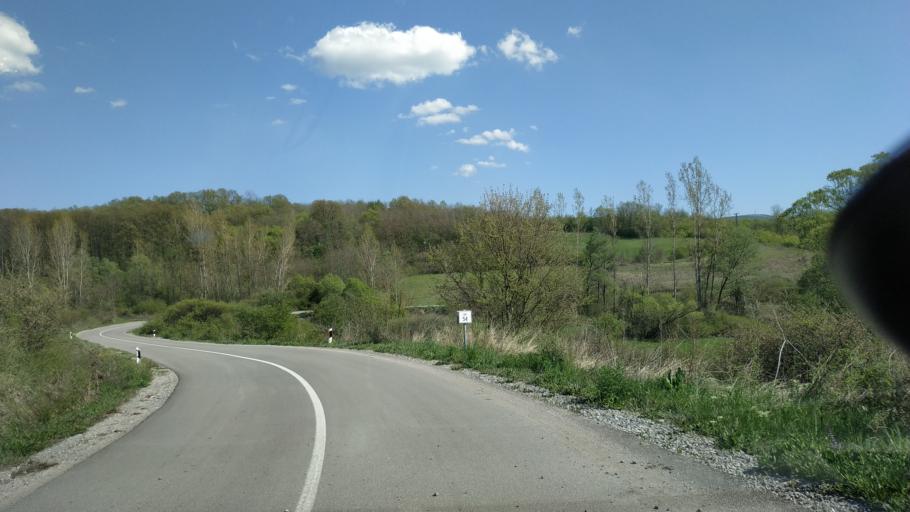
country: RS
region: Central Serbia
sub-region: Zajecarski Okrug
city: Soko Banja
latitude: 43.4822
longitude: 21.8691
